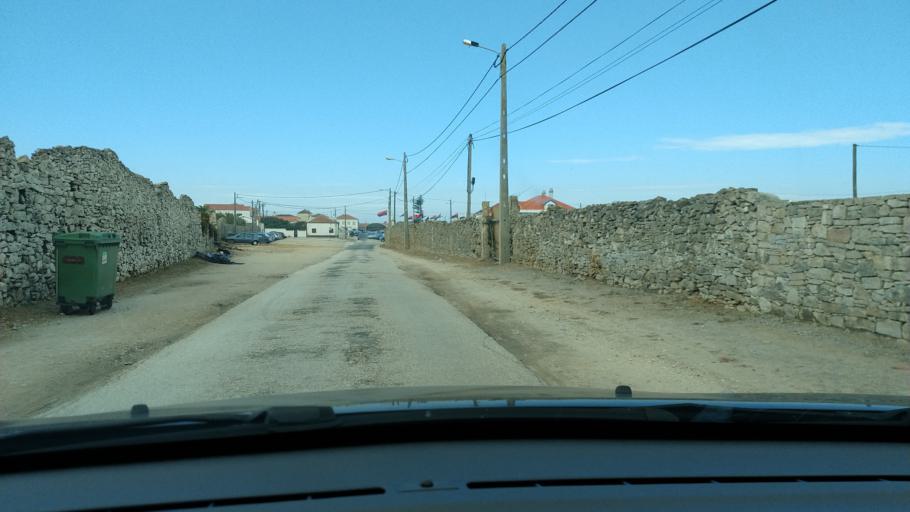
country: PT
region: Leiria
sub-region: Peniche
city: Peniche
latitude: 39.3654
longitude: -9.3995
